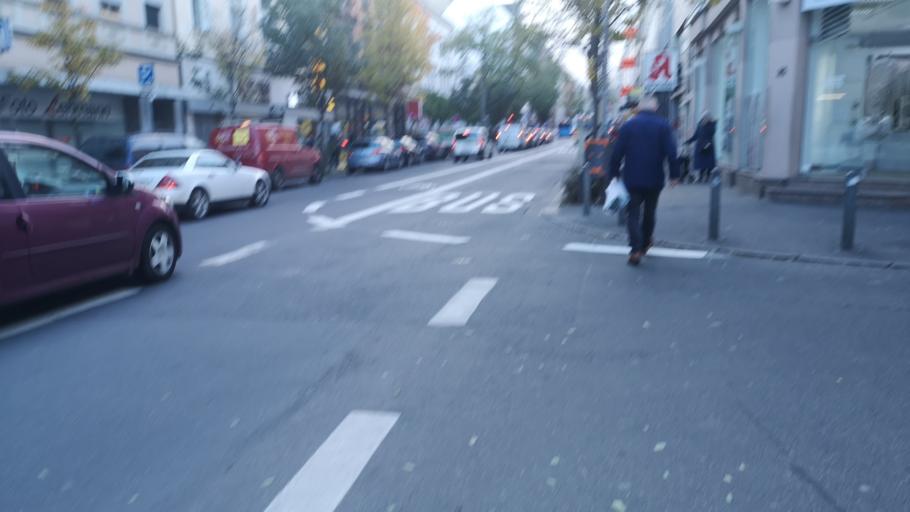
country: DE
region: Hesse
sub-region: Regierungsbezirk Darmstadt
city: Wiesbaden
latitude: 50.0806
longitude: 8.2317
